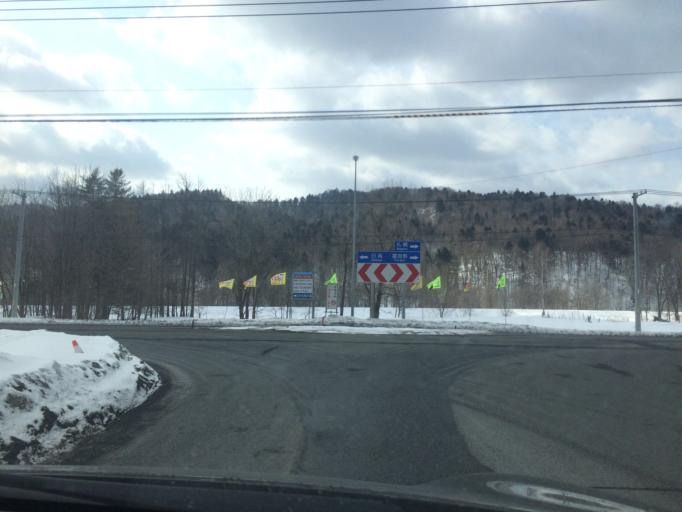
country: JP
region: Hokkaido
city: Shimo-furano
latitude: 42.9758
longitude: 142.4117
